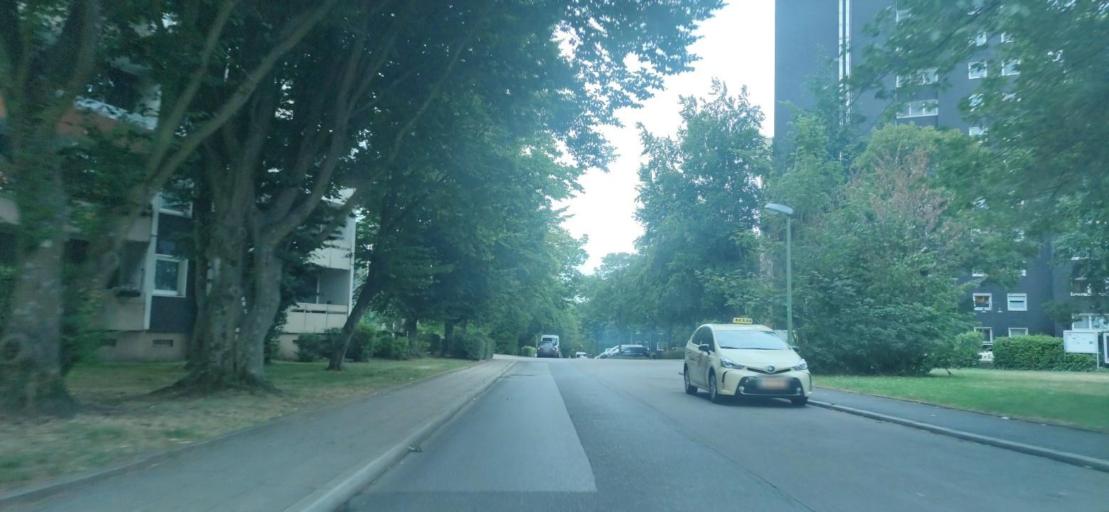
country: DE
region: North Rhine-Westphalia
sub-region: Regierungsbezirk Dusseldorf
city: Essen
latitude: 51.4183
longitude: 7.0803
